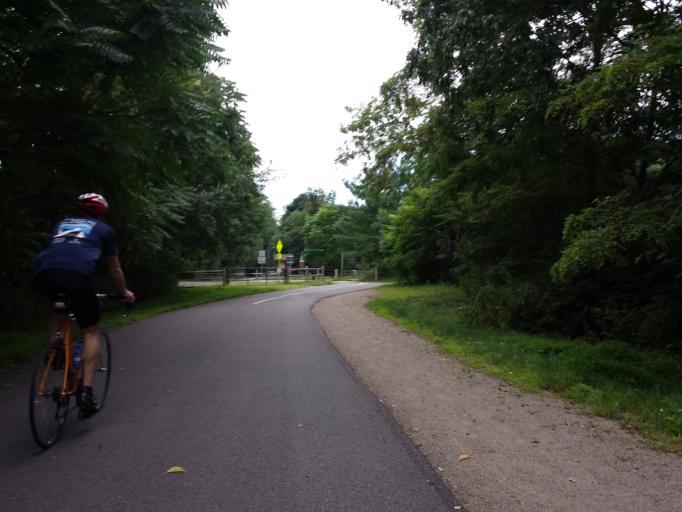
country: US
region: New York
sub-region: Dutchess County
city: Myers Corner
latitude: 41.6025
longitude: -73.8363
